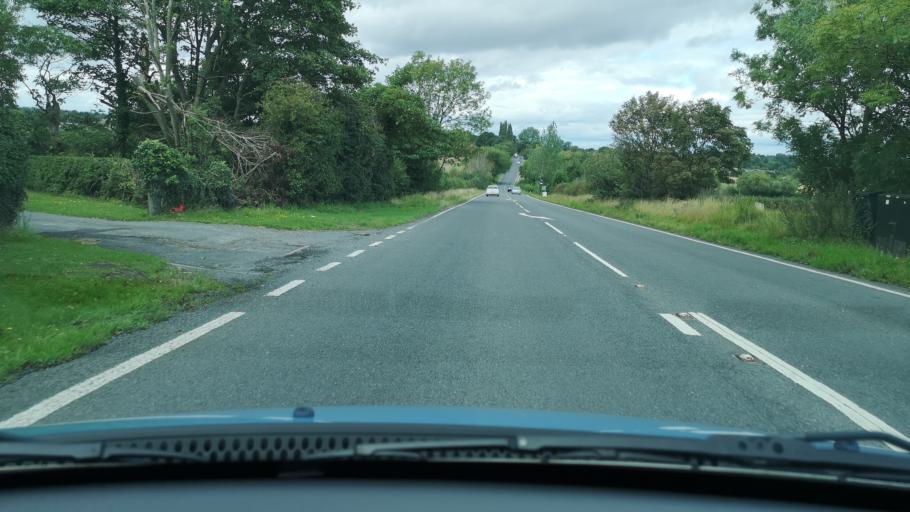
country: GB
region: England
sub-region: City and Borough of Wakefield
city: Low Ackworth
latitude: 53.6354
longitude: -1.3262
